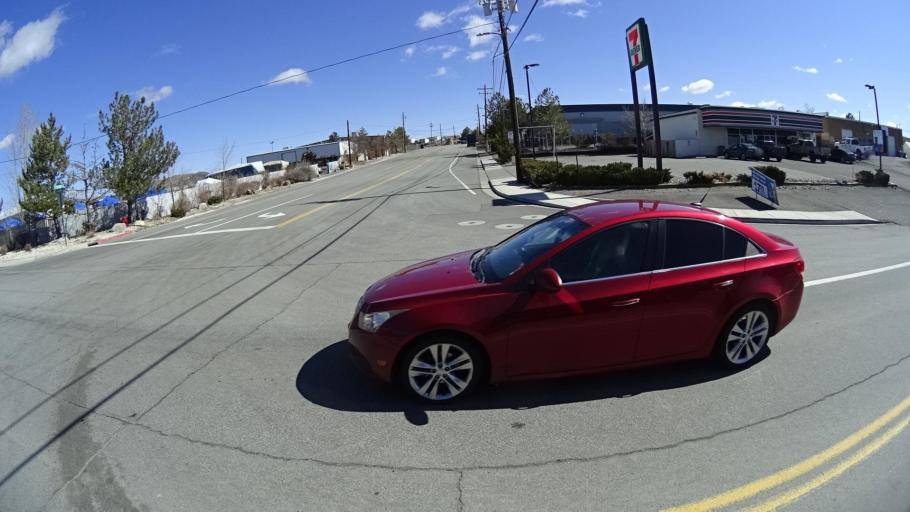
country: US
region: Nevada
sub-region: Washoe County
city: Golden Valley
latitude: 39.5918
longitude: -119.8358
